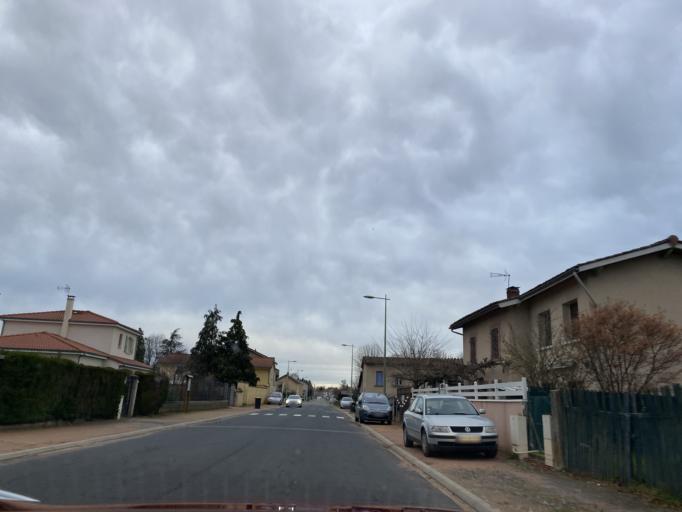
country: FR
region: Auvergne
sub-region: Departement du Puy-de-Dome
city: Peschadoires
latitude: 45.8331
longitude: 3.5003
